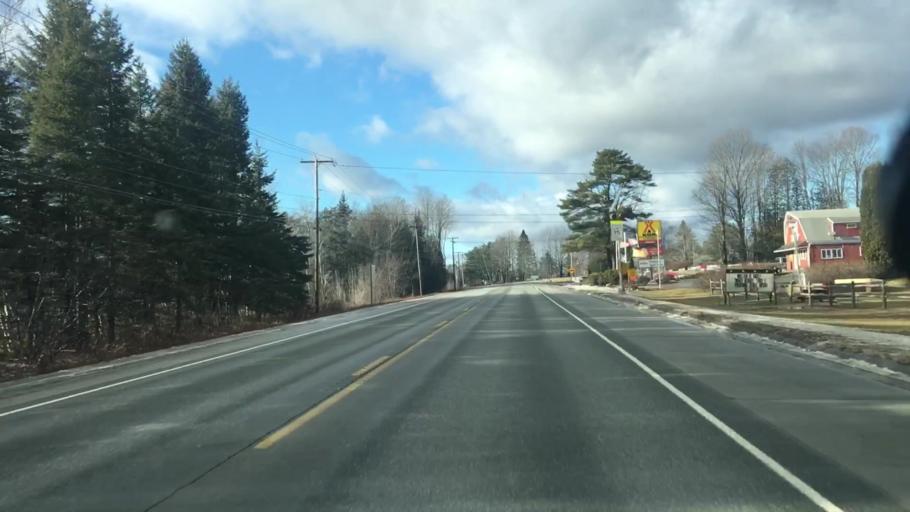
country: US
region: Maine
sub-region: Penobscot County
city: Holden
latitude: 44.7540
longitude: -68.6592
